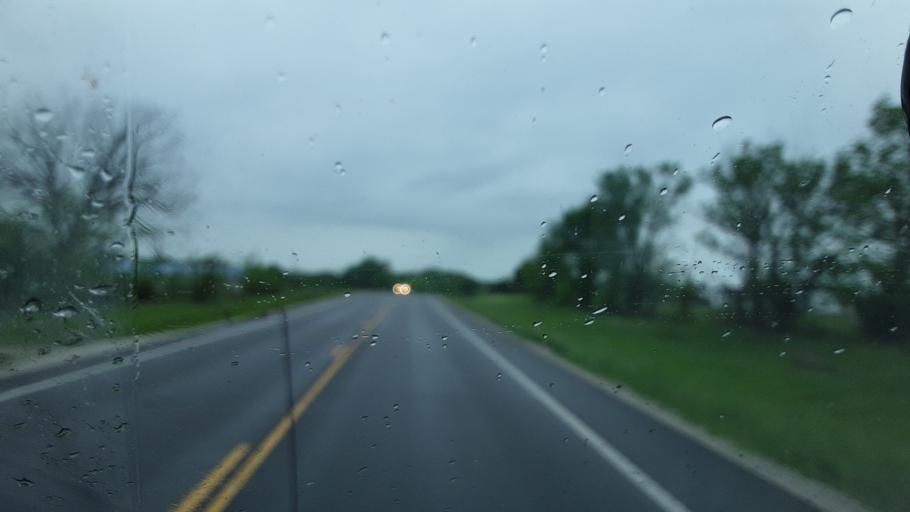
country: US
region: Missouri
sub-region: Monroe County
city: Paris
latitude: 39.4804
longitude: -92.1159
